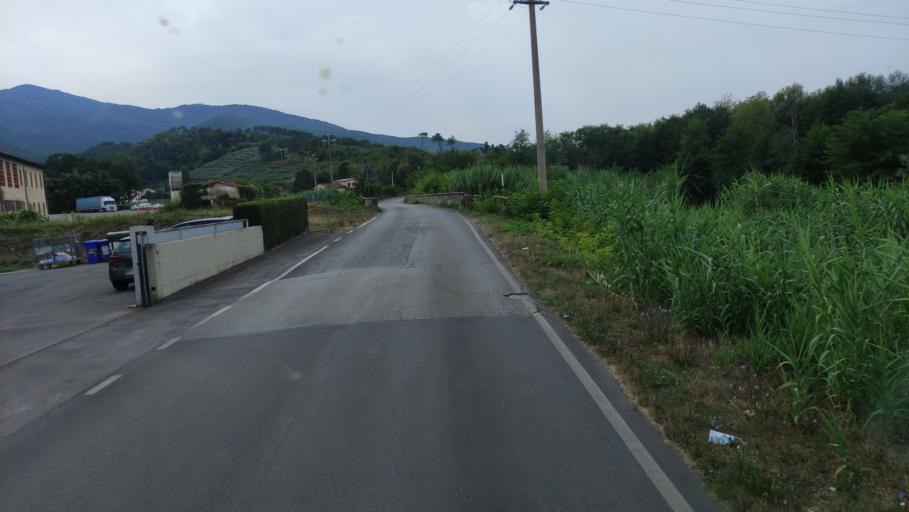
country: IT
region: Tuscany
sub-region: Provincia di Lucca
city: Lucca
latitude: 43.8055
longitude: 10.4970
